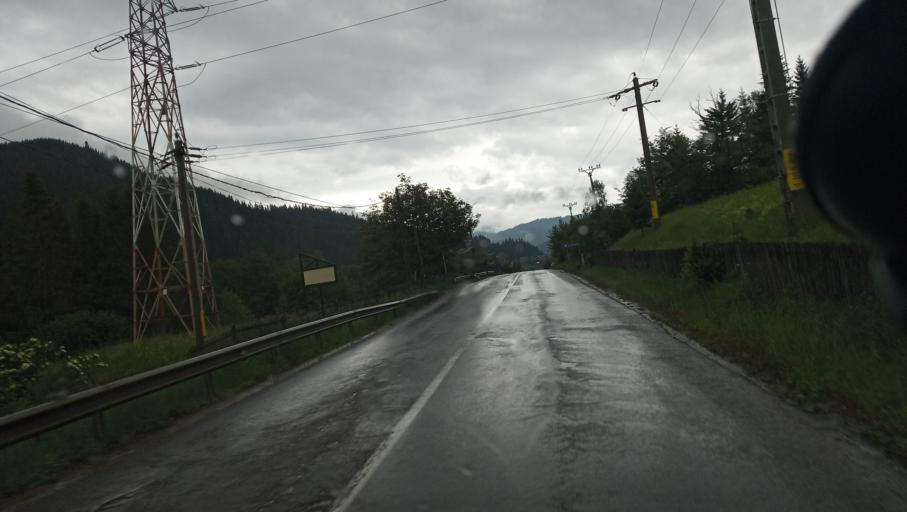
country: RO
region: Neamt
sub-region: Comuna Poiana Teiului
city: Poiana Teiului
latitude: 47.0902
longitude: 25.9712
